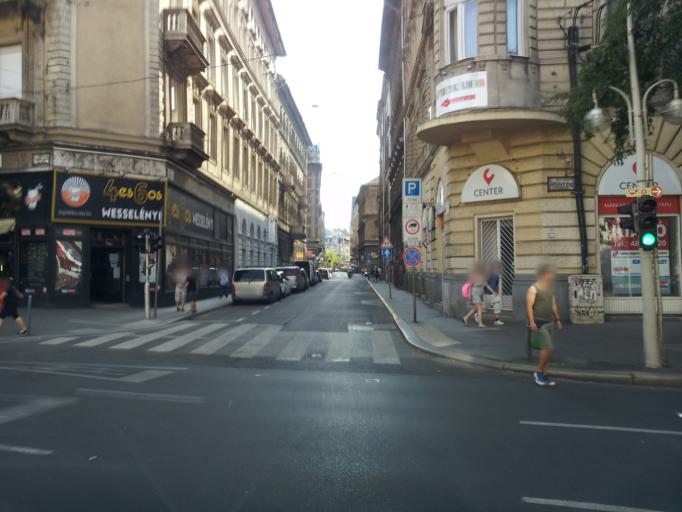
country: HU
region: Budapest
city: Budapest VII. keruelet
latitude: 47.5006
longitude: 19.0687
